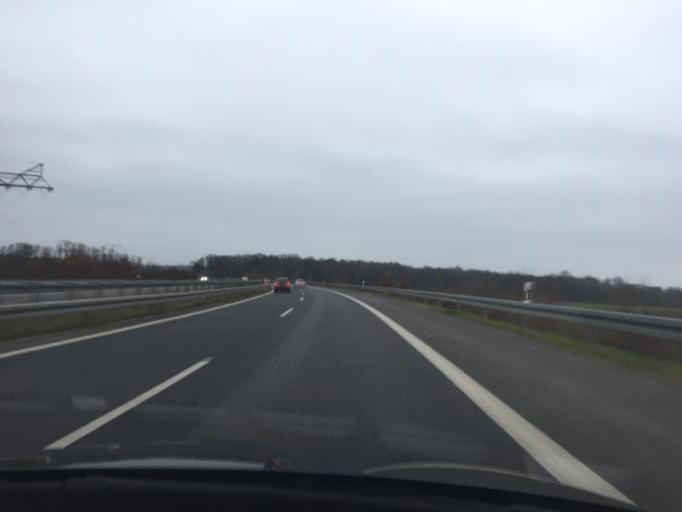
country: DE
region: Brandenburg
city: Rangsdorf
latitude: 52.3292
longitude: 13.4449
